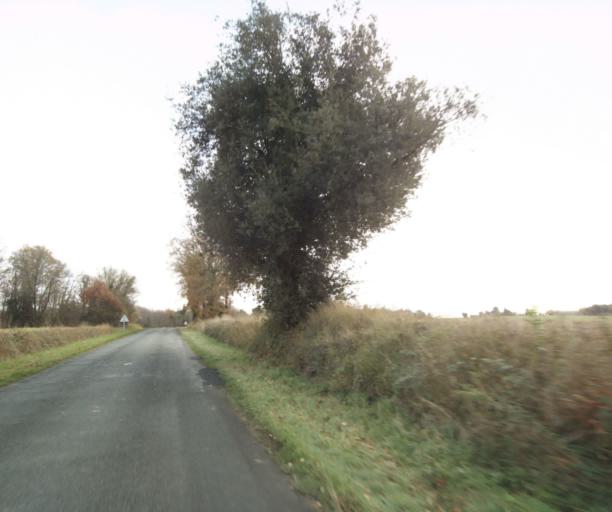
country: FR
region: Poitou-Charentes
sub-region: Departement de la Charente-Maritime
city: Corme-Royal
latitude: 45.7888
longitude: -0.8308
